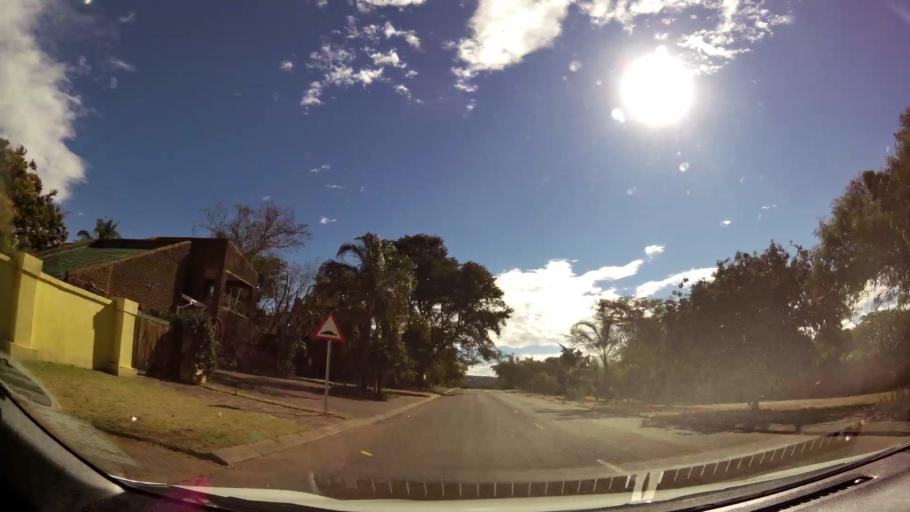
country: ZA
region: Limpopo
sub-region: Waterberg District Municipality
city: Warmbaths
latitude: -24.8722
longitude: 28.2902
